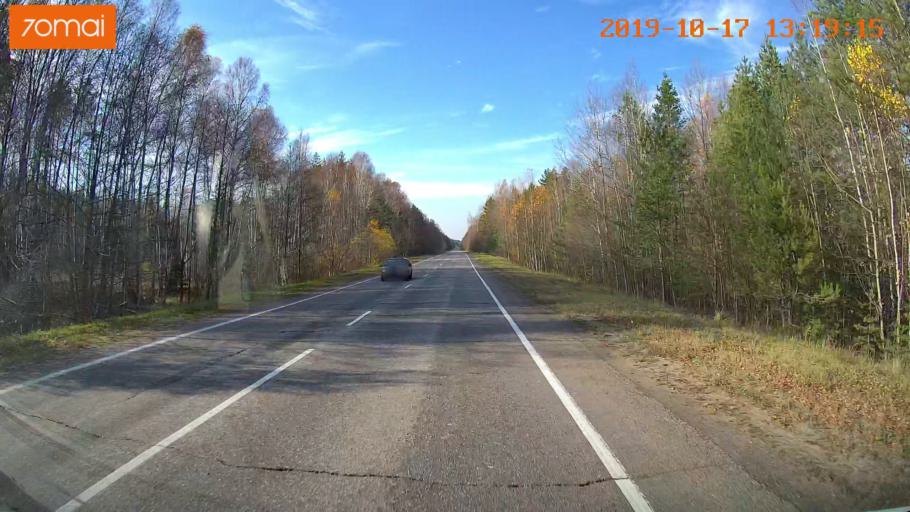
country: RU
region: Rjazan
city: Gus'-Zheleznyy
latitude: 55.0682
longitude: 41.0785
